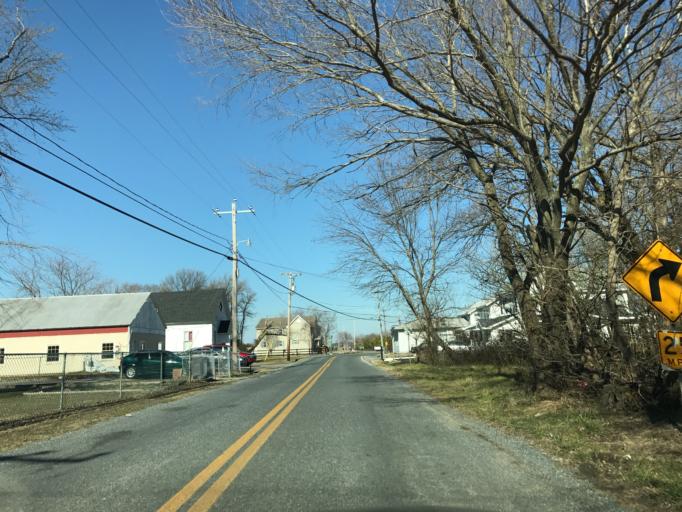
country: US
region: Maryland
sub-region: Queen Anne's County
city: Chester
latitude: 38.9463
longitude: -76.2814
